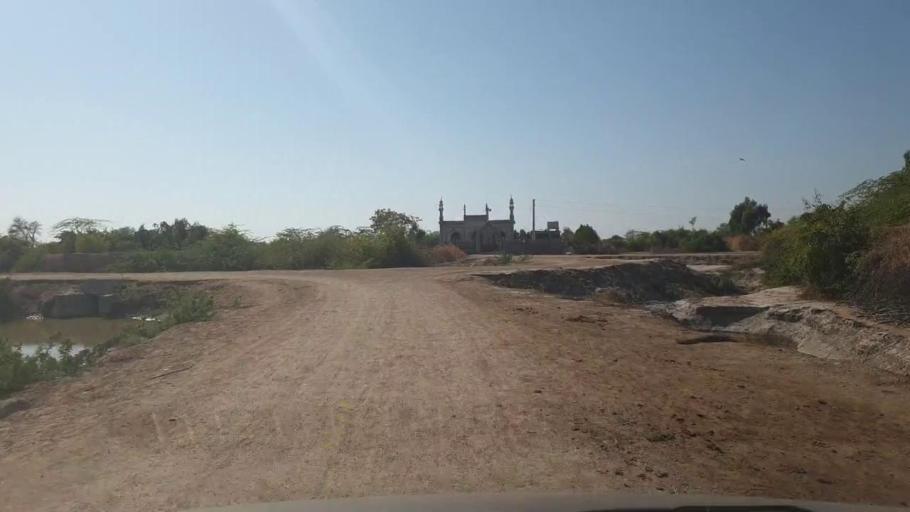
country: PK
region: Sindh
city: Dhoro Naro
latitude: 25.4070
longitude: 69.5873
